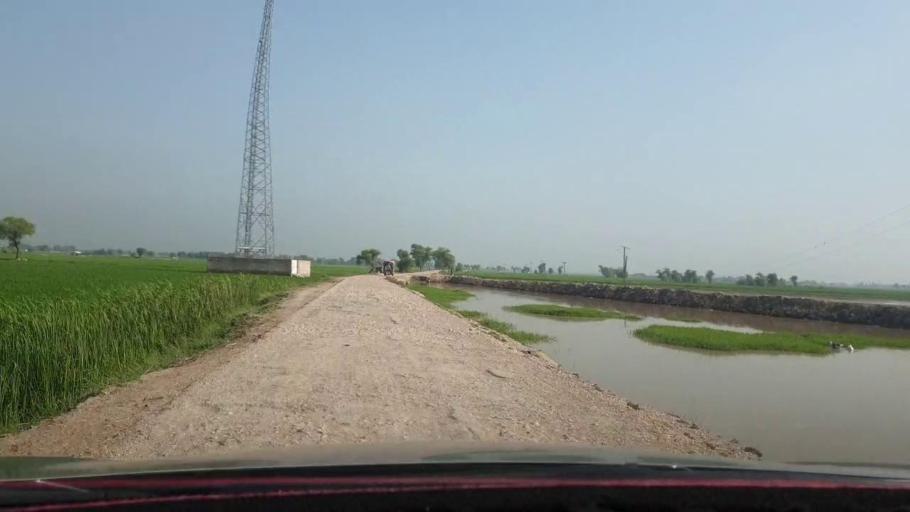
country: PK
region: Sindh
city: Nasirabad
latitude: 27.4856
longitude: 67.9258
